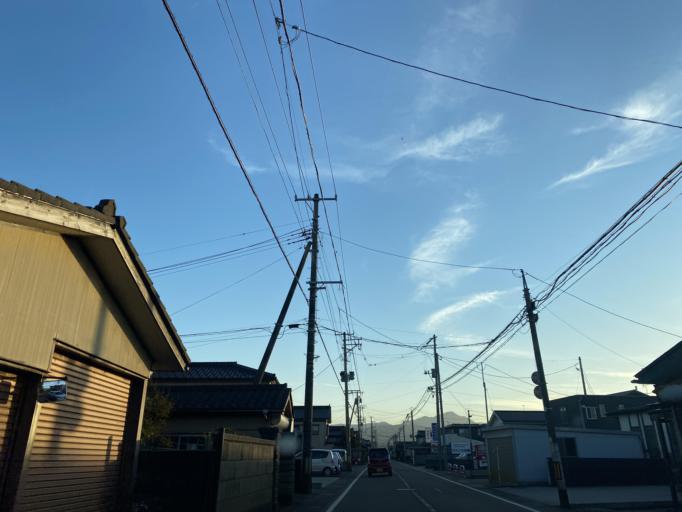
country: JP
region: Niigata
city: Kashiwazaki
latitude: 37.3795
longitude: 138.5669
